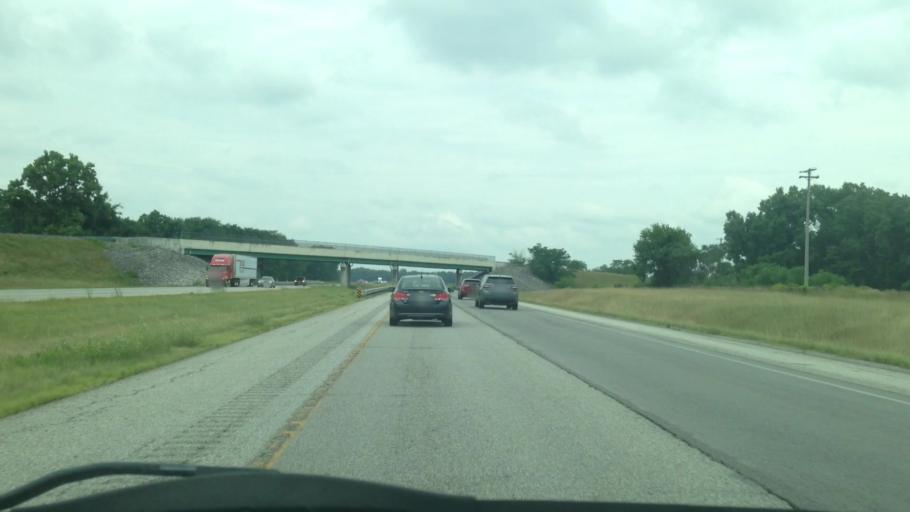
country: US
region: Michigan
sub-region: Saint Joseph County
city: White Pigeon
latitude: 41.7504
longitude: -85.5618
